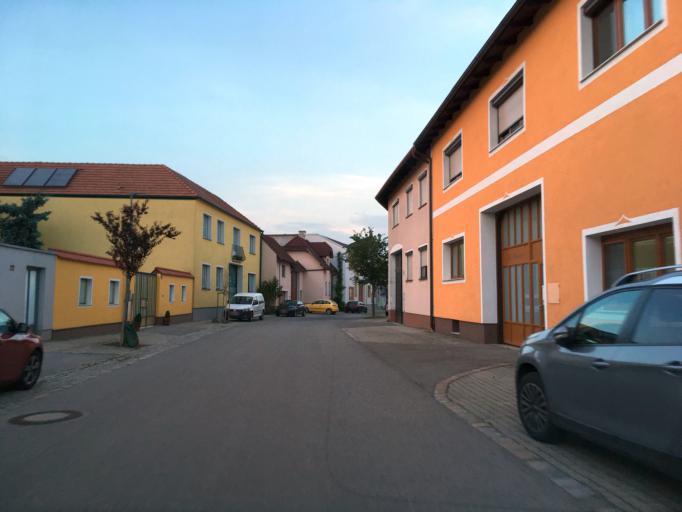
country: AT
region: Lower Austria
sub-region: Politischer Bezirk Baden
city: Teesdorf
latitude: 47.9512
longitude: 16.2773
